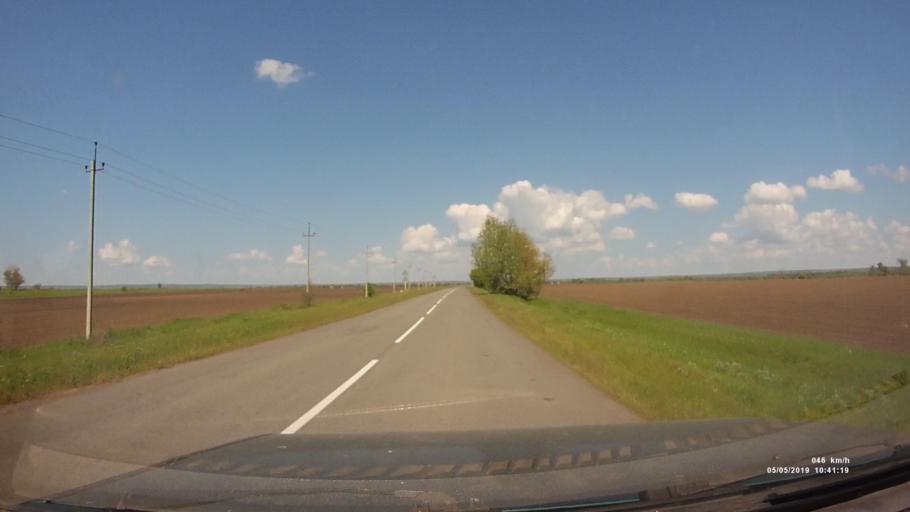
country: RU
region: Rostov
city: Ust'-Donetskiy
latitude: 47.5902
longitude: 40.8432
